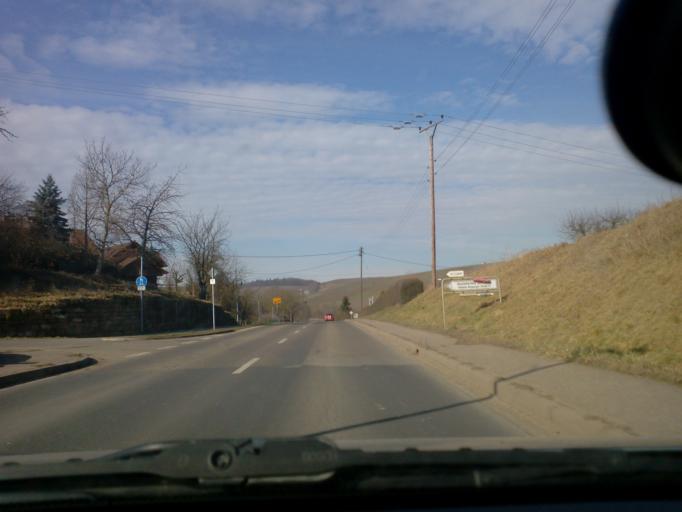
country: DE
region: Baden-Wuerttemberg
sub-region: Regierungsbezirk Stuttgart
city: Brackenheim
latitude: 49.0834
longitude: 9.0611
